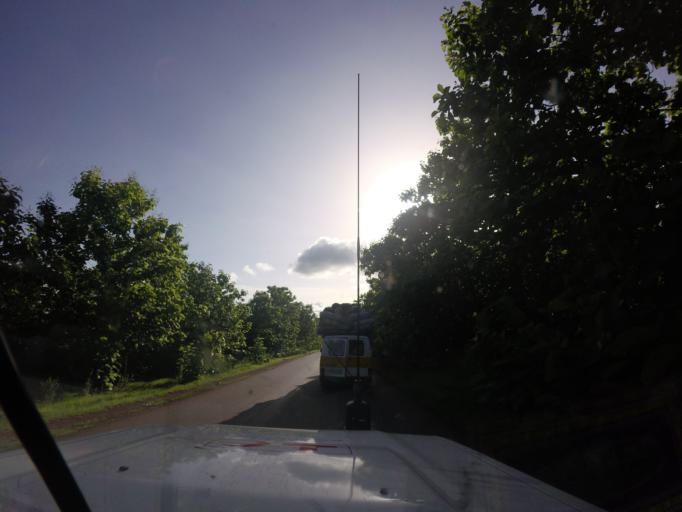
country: GN
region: Kindia
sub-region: Kindia
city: Kindia
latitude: 9.9910
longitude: -12.7450
